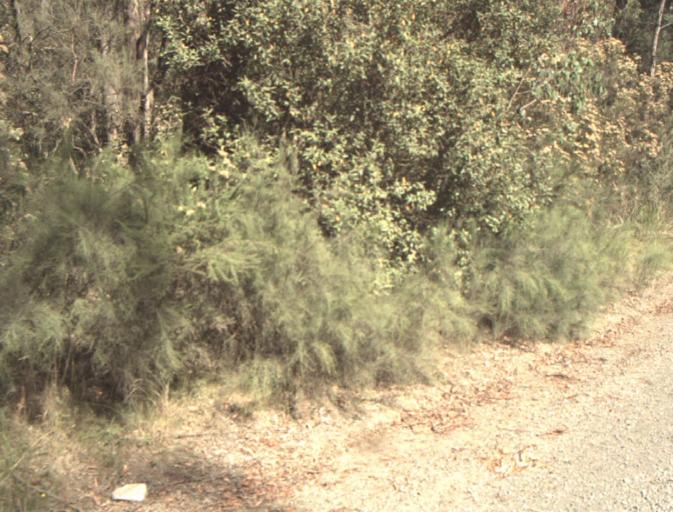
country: AU
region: Tasmania
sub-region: Launceston
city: Newstead
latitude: -41.3712
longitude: 147.2785
